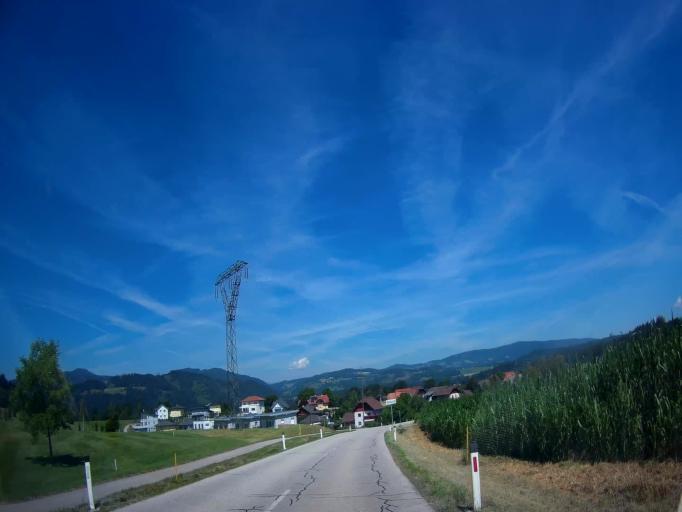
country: AT
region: Carinthia
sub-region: Politischer Bezirk Sankt Veit an der Glan
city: St. Georgen am Laengsee
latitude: 46.7977
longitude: 14.4146
